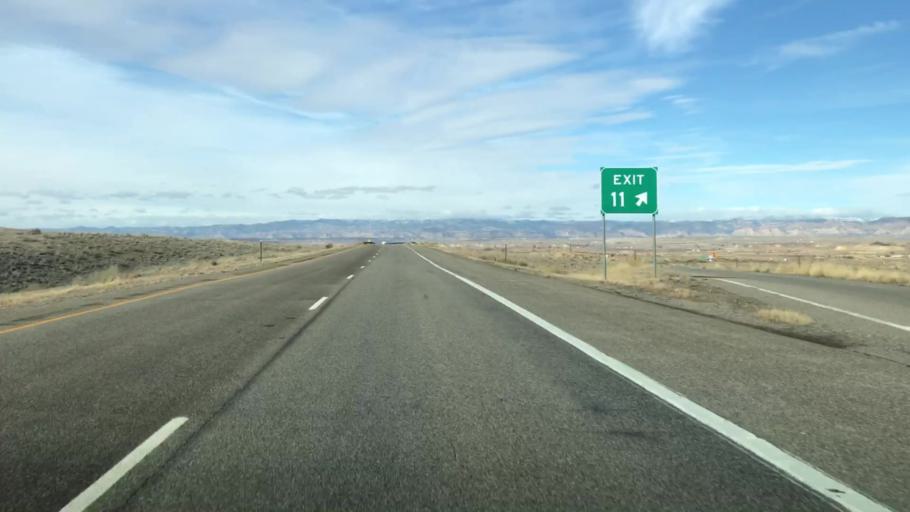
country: US
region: Colorado
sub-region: Mesa County
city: Loma
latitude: 39.2123
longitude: -108.8652
